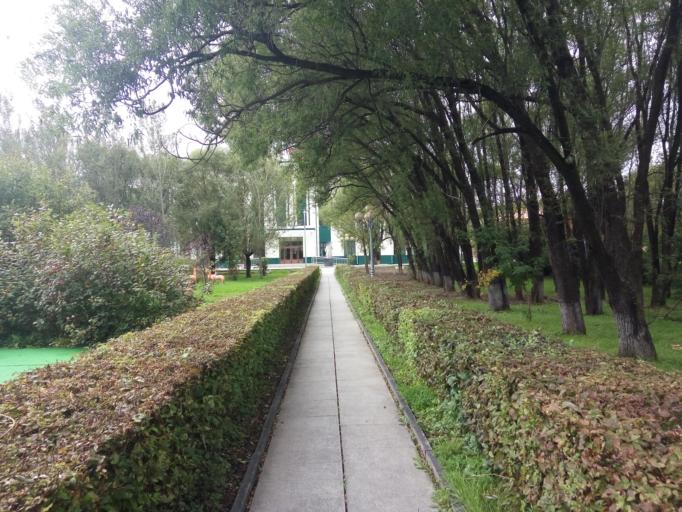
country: CN
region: Heilongjiang Sheng
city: Erjing
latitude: 48.6504
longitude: 126.1412
